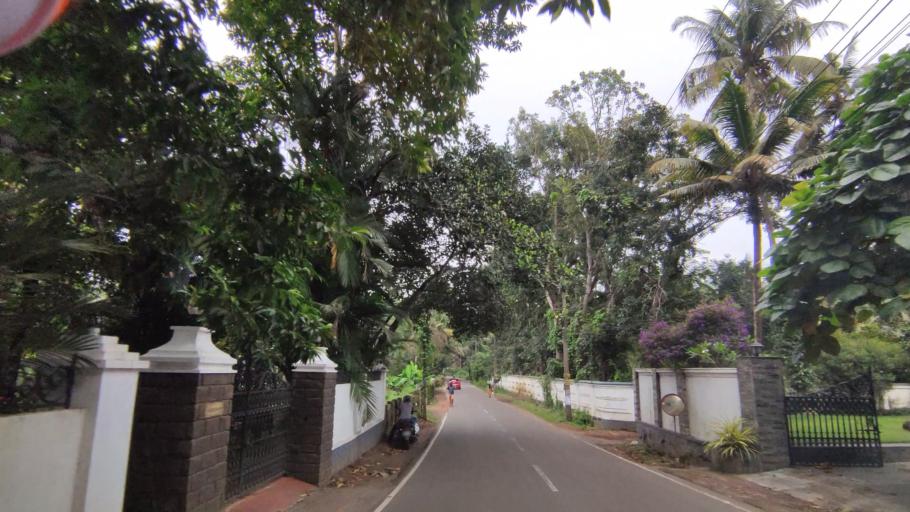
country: IN
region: Kerala
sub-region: Kottayam
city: Kottayam
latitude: 9.6569
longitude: 76.5288
